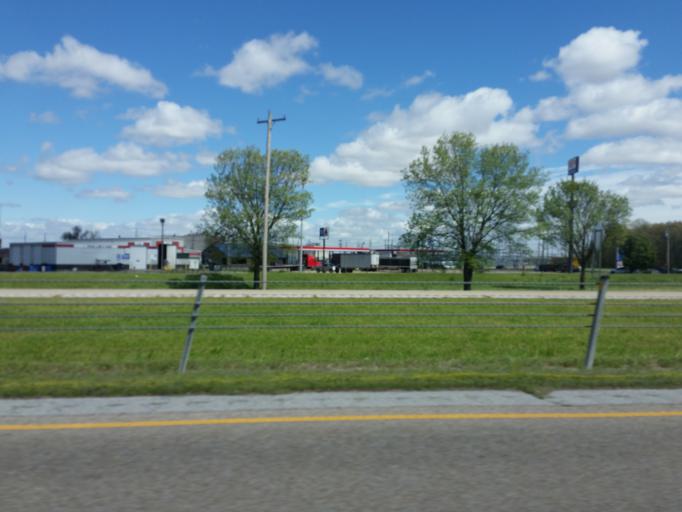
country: US
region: Arkansas
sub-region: Craighead County
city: Jonesboro
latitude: 35.8033
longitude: -90.6272
